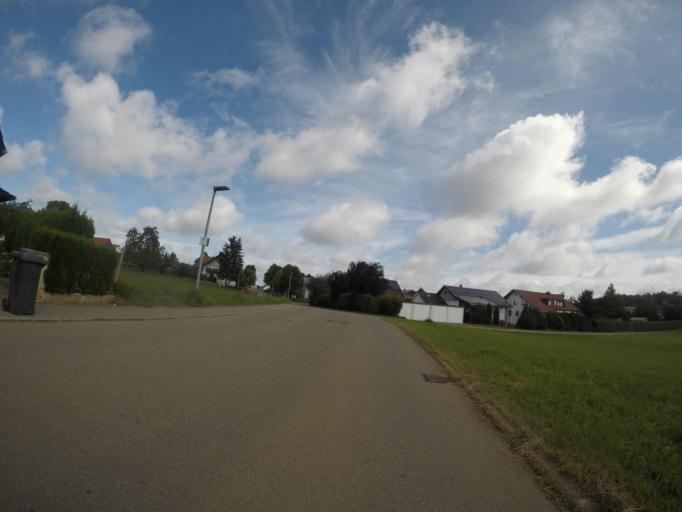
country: DE
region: Baden-Wuerttemberg
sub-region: Tuebingen Region
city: Laichingen
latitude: 48.4407
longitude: 9.6561
